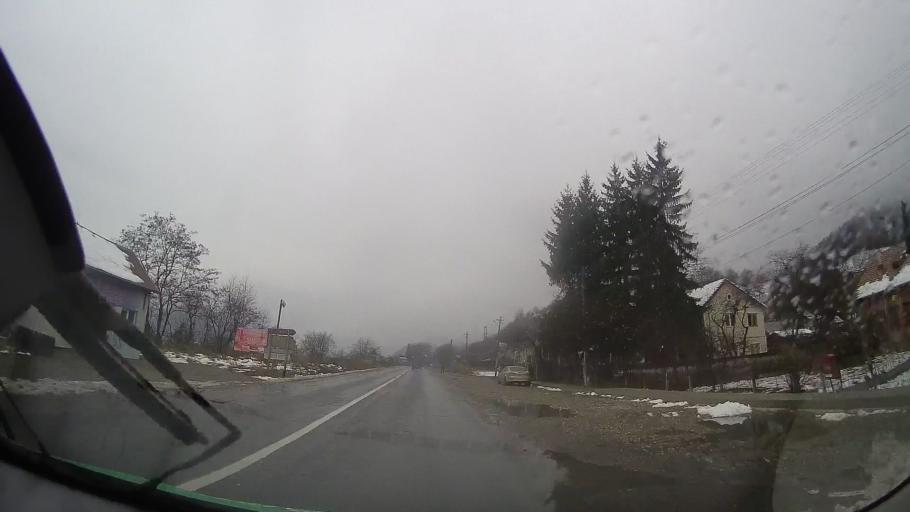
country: RO
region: Neamt
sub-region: Comuna Alexandru Cel Bun
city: Vadurele
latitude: 46.9412
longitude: 26.2718
